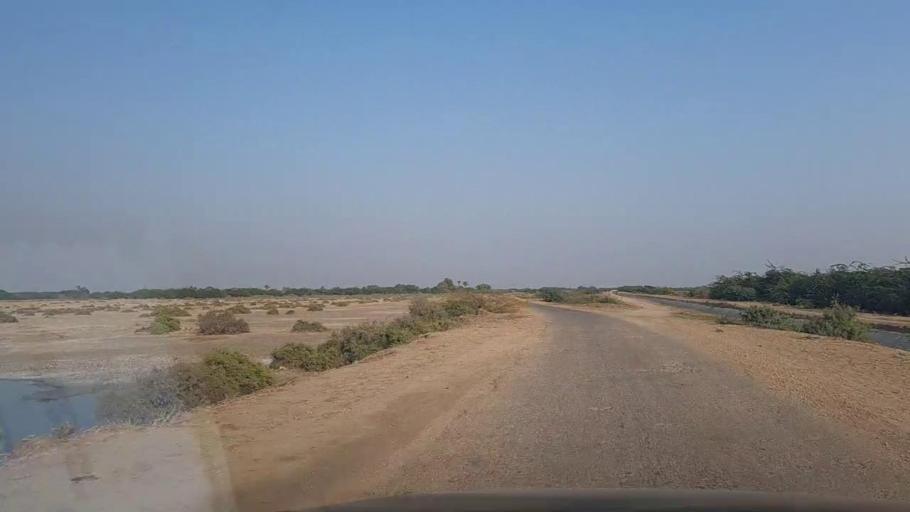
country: PK
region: Sindh
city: Keti Bandar
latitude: 24.2652
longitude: 67.5554
